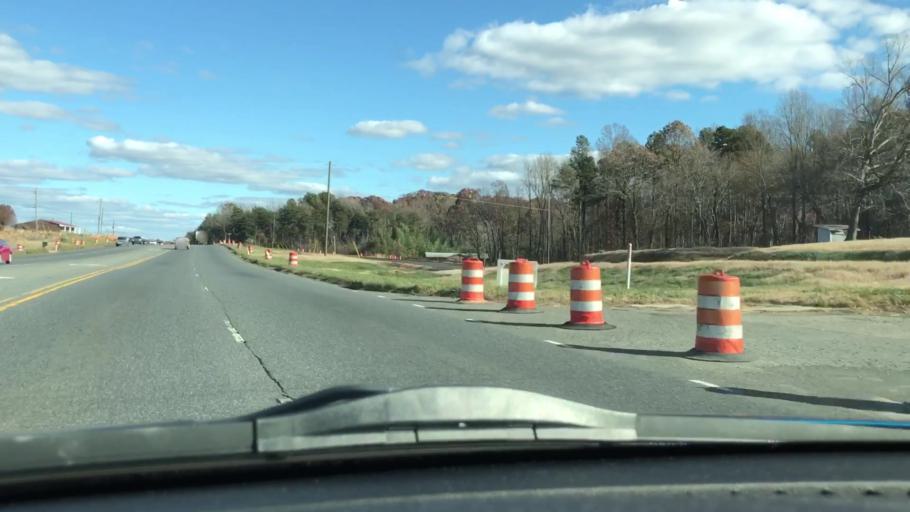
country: US
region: North Carolina
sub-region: Randolph County
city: Franklinville
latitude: 35.7242
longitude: -79.7482
